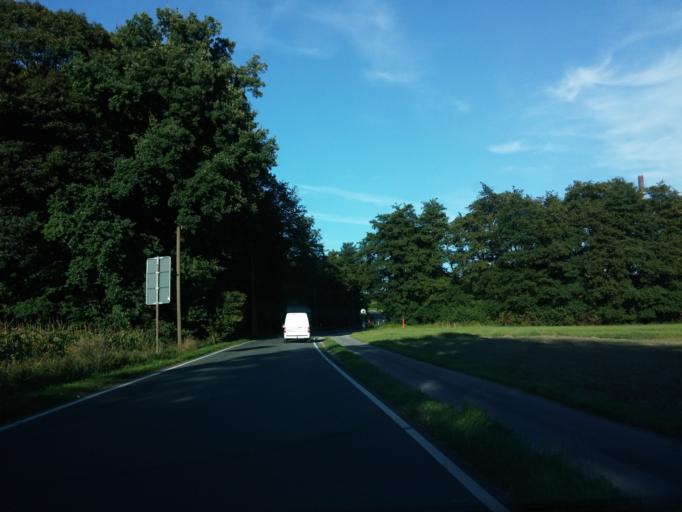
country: DE
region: North Rhine-Westphalia
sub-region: Regierungsbezirk Munster
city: Gladbeck
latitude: 51.6071
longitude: 6.9790
